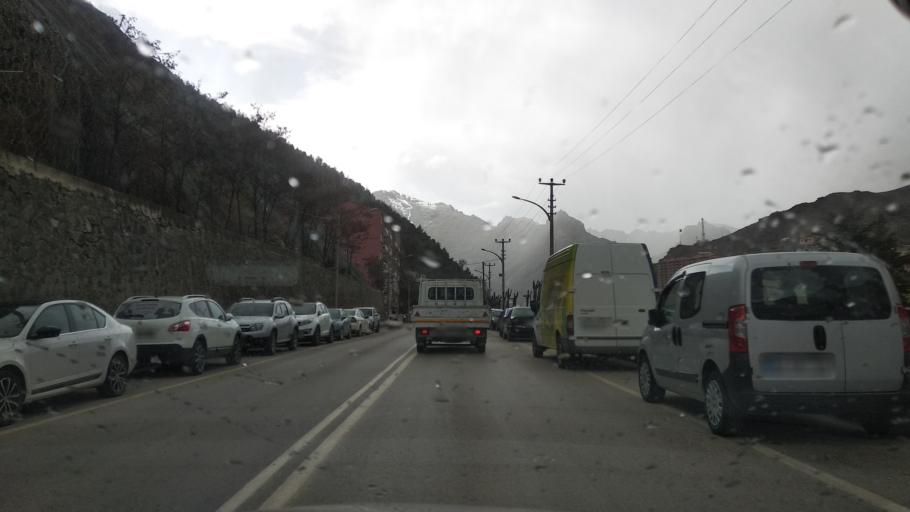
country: TR
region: Gumushane
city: Gumushkhane
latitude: 40.4584
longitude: 39.4777
